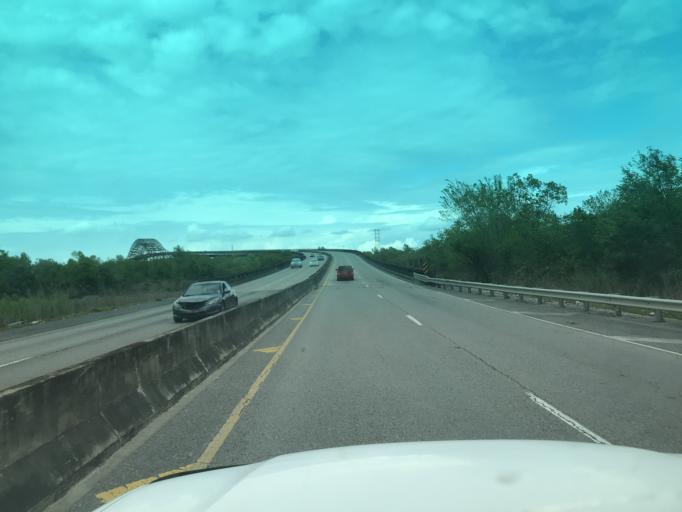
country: US
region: Louisiana
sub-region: Saint Bernard Parish
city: Chalmette
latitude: 29.9958
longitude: -89.9401
